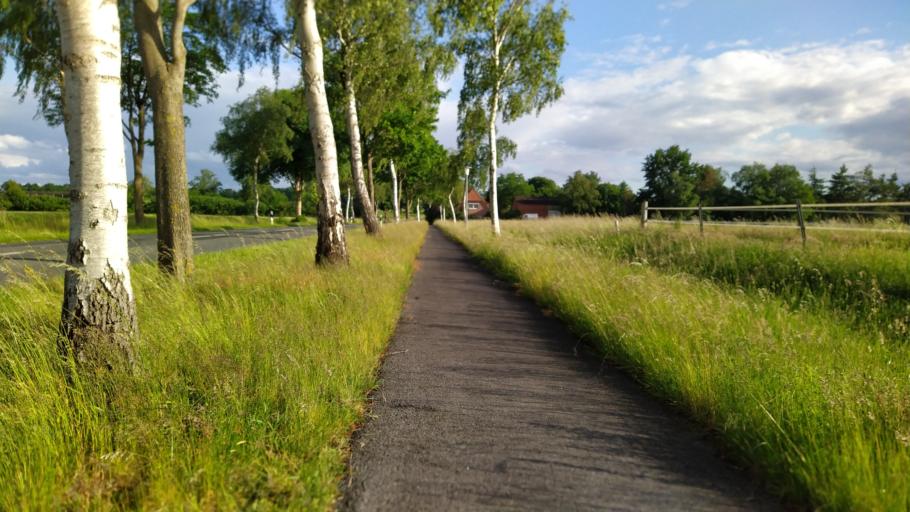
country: DE
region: Lower Saxony
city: Brest
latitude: 53.4581
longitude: 9.3838
